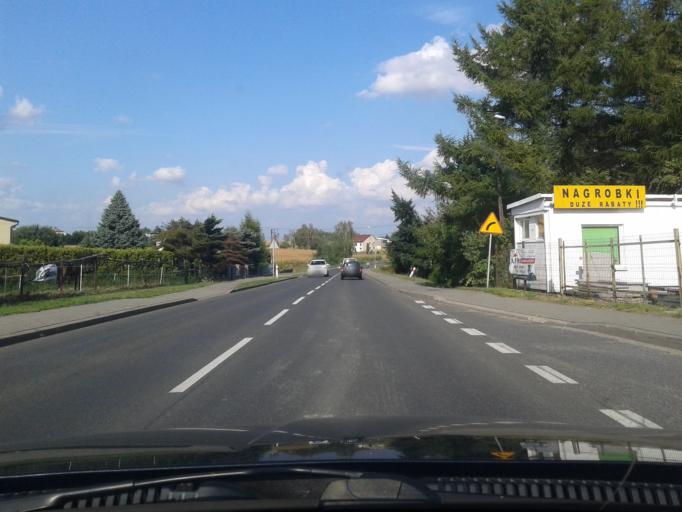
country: PL
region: Silesian Voivodeship
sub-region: Powiat wodzislawski
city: Gorzyce
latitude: 49.9606
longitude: 18.4024
